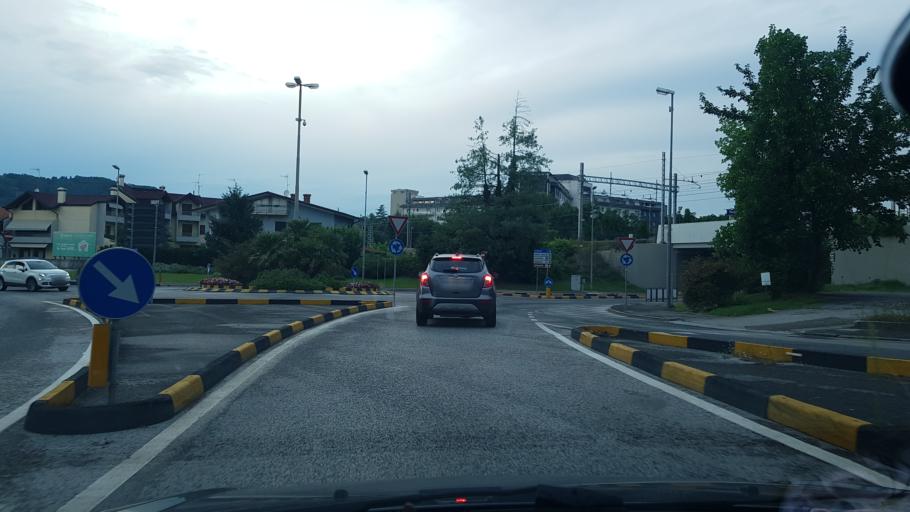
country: IT
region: Friuli Venezia Giulia
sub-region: Provincia di Gorizia
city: Gorizia
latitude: 45.9331
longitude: 13.6057
